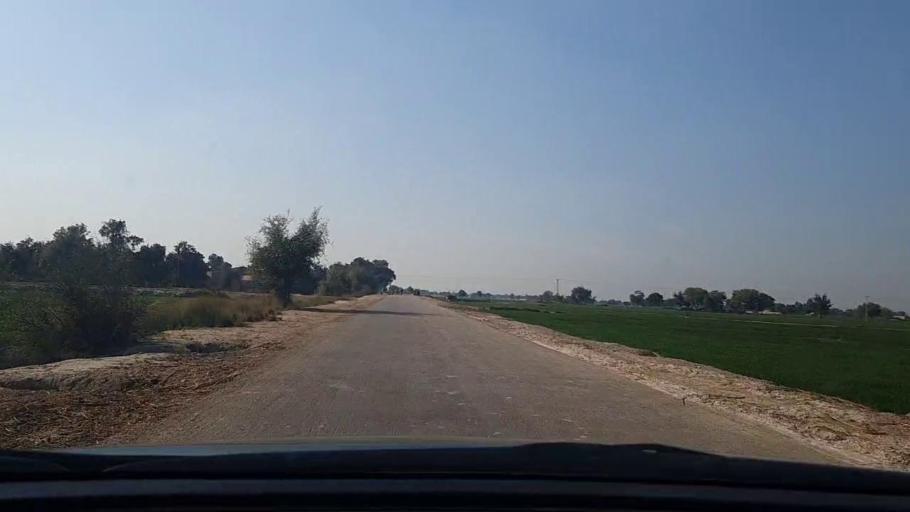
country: PK
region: Sindh
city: Daulatpur
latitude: 26.3173
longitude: 68.0585
